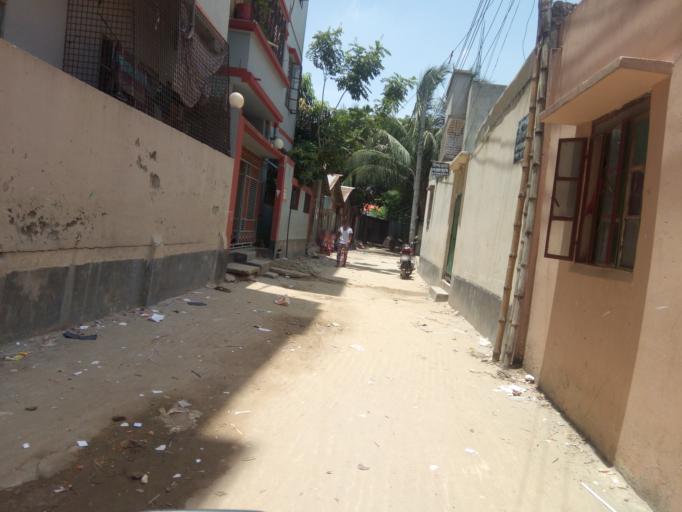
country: BD
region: Dhaka
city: Paltan
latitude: 23.7590
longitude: 90.4389
